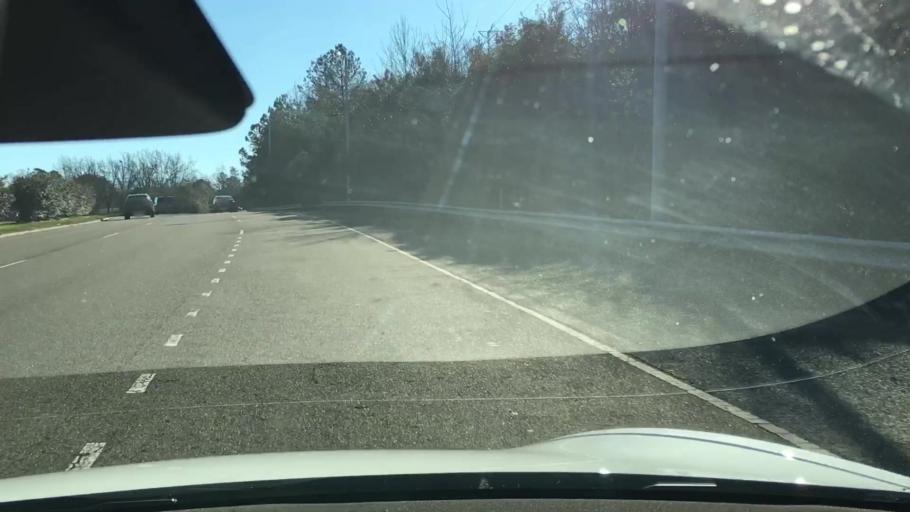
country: US
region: Virginia
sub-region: Chesterfield County
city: Bon Air
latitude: 37.5453
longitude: -77.5580
